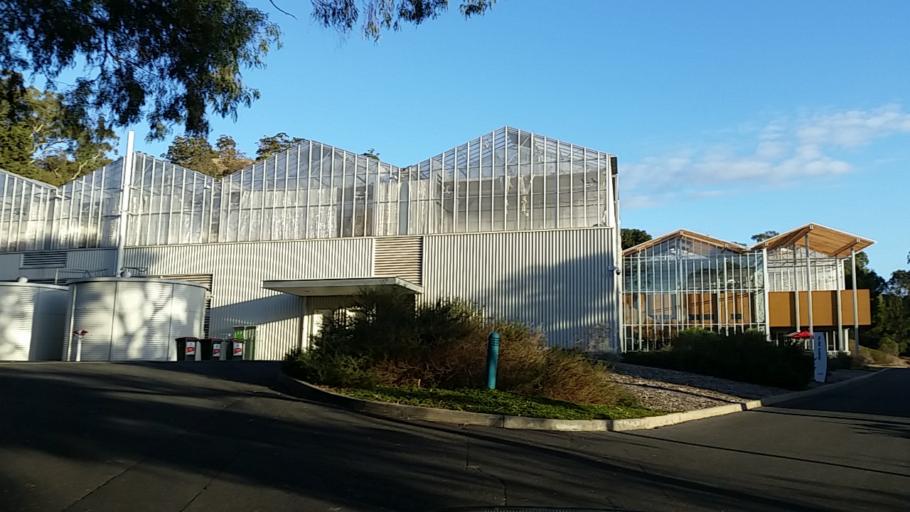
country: AU
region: South Australia
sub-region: Burnside
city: Mount Osmond
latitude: -34.9707
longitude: 138.6397
